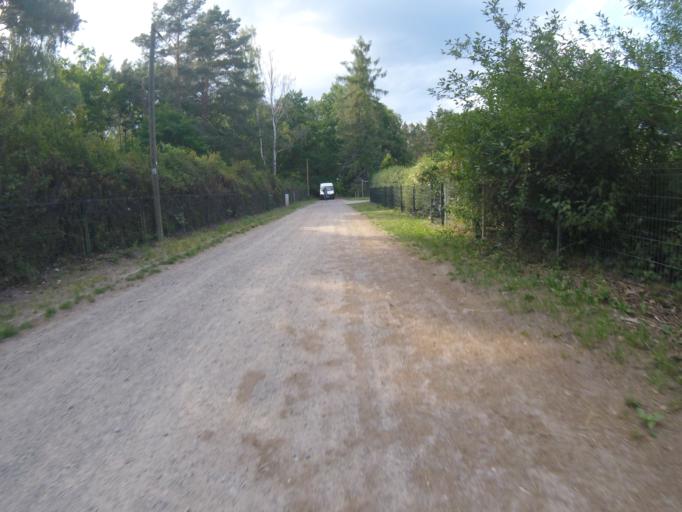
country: DE
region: Brandenburg
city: Bestensee
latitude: 52.2629
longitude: 13.6136
